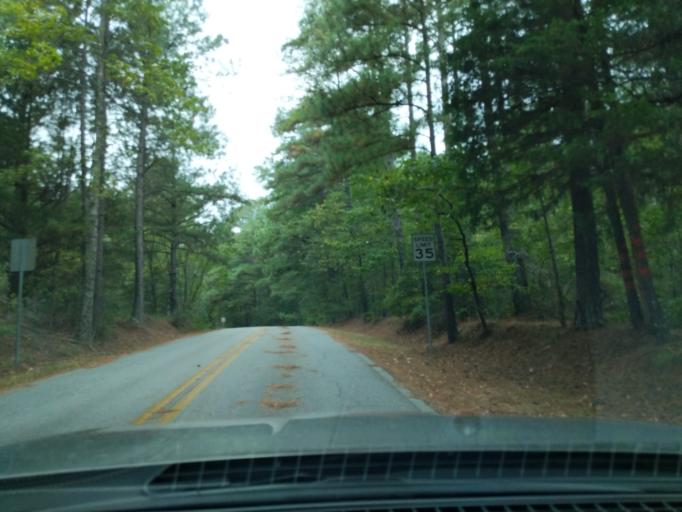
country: US
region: Georgia
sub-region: Columbia County
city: Appling
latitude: 33.6420
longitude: -82.3858
